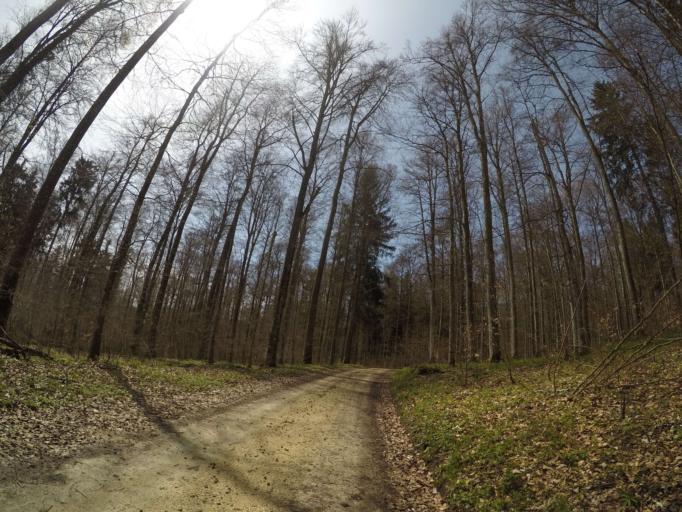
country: DE
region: Baden-Wuerttemberg
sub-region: Regierungsbezirk Stuttgart
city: Neidlingen
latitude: 48.5393
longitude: 9.5738
